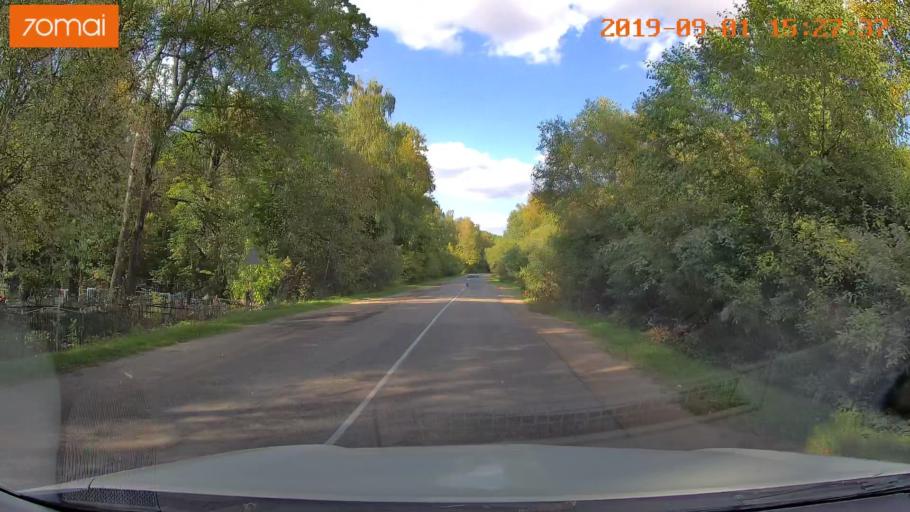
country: RU
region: Kaluga
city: Maloyaroslavets
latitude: 54.9760
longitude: 36.4673
